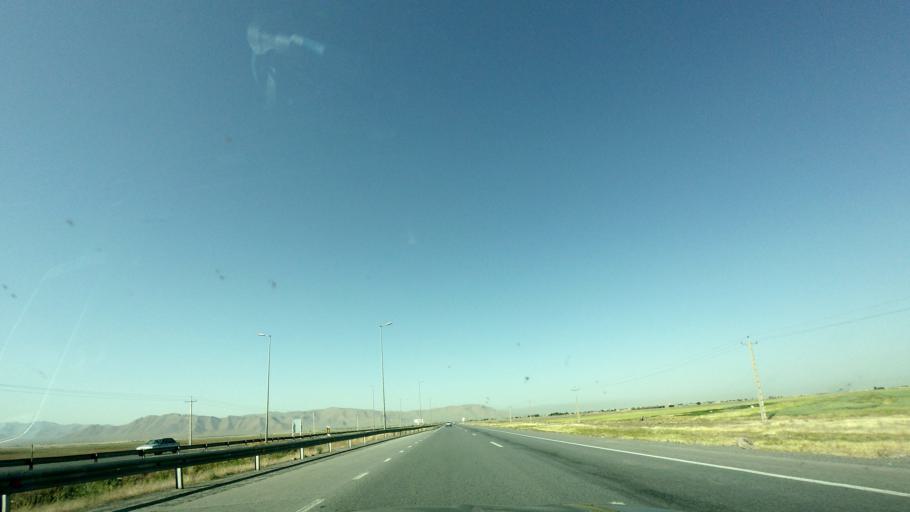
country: IR
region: Markazi
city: Ashtian
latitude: 34.1811
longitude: 50.0455
